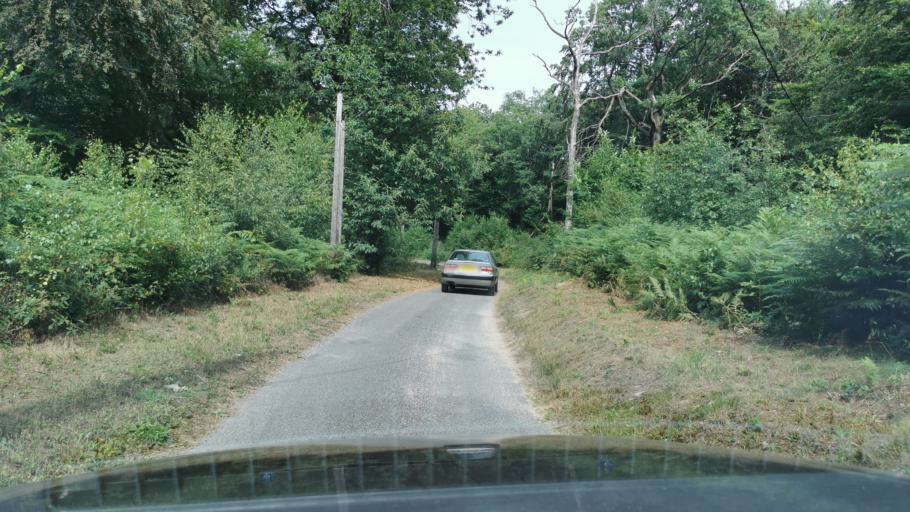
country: FR
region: Bourgogne
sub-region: Departement de Saone-et-Loire
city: Marmagne
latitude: 46.8018
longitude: 4.2711
